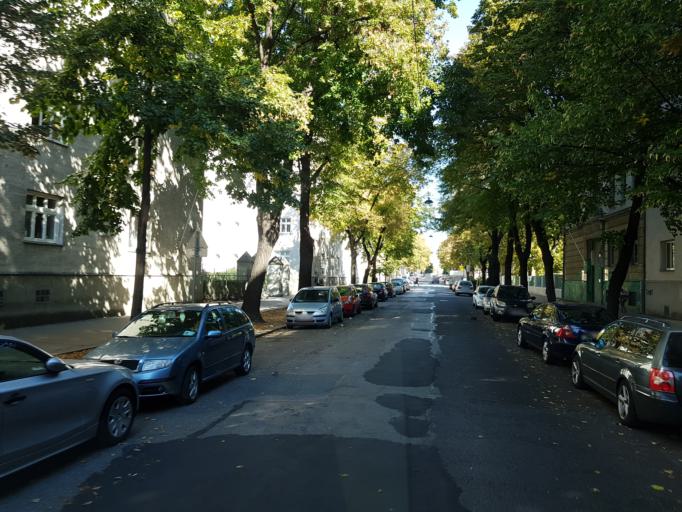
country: AT
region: Vienna
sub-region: Wien Stadt
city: Vienna
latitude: 48.2409
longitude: 16.3804
